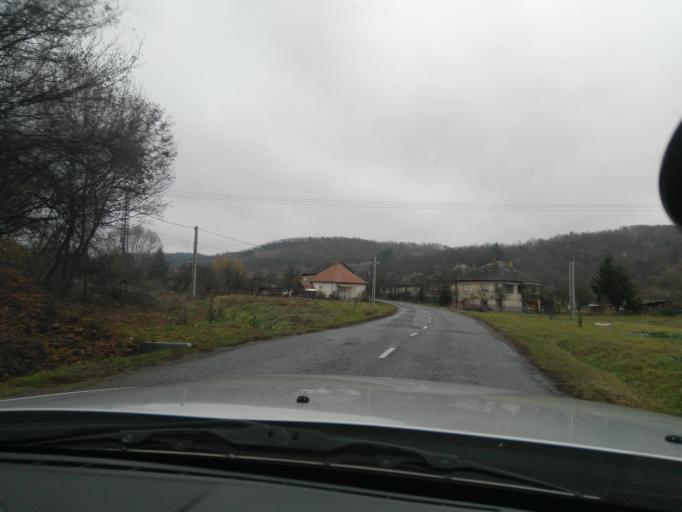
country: HU
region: Nograd
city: Kazar
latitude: 48.0475
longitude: 19.8998
